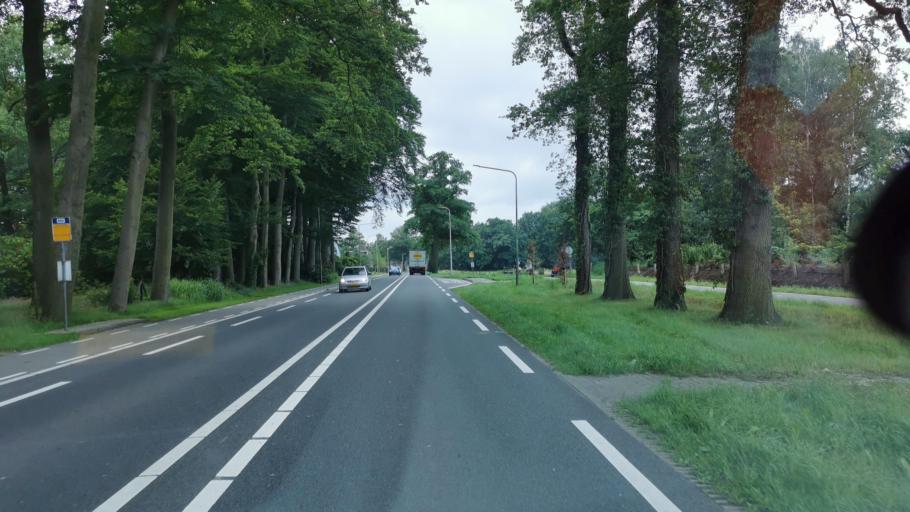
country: NL
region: Overijssel
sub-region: Gemeente Enschede
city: Enschede
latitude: 52.2370
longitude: 6.9113
